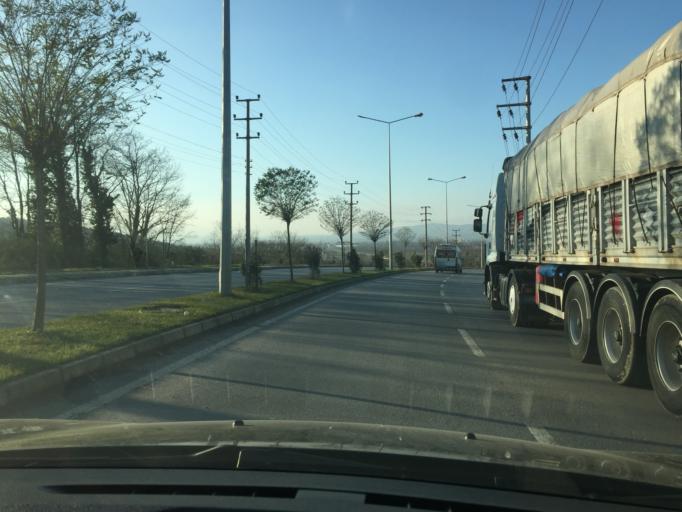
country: TR
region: Sakarya
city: Sogutlu
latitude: 40.8992
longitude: 30.5076
